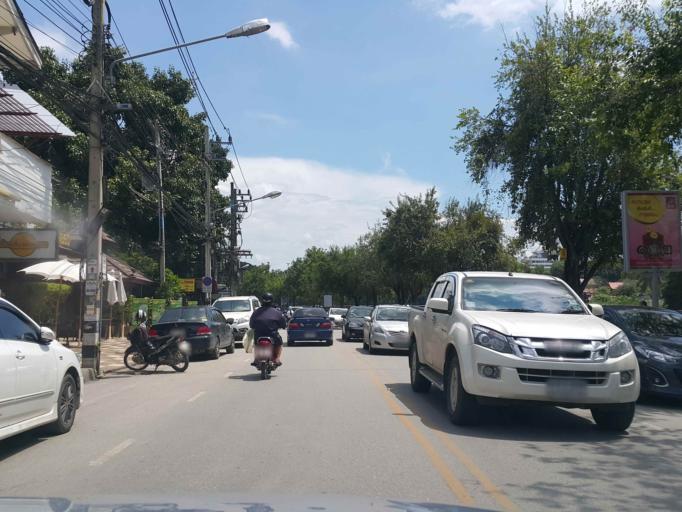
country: TH
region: Chiang Mai
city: Chiang Mai
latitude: 18.7857
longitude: 99.0051
